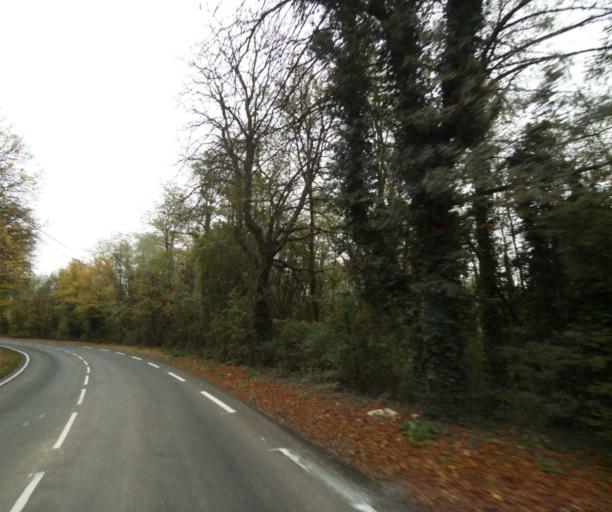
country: FR
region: Lorraine
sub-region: Departement de Meurthe-et-Moselle
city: Joeuf
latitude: 49.2320
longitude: 6.0261
